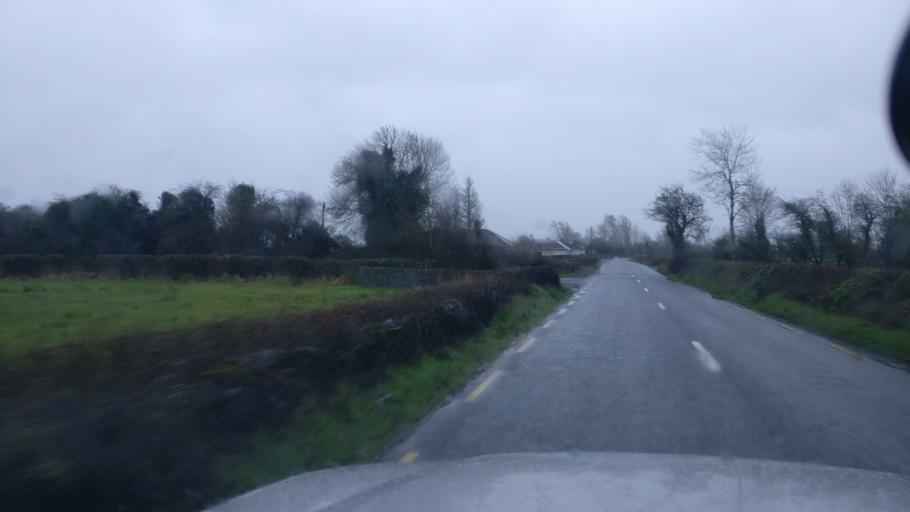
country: IE
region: Connaught
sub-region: County Galway
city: Ballinasloe
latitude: 53.2777
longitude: -8.2120
